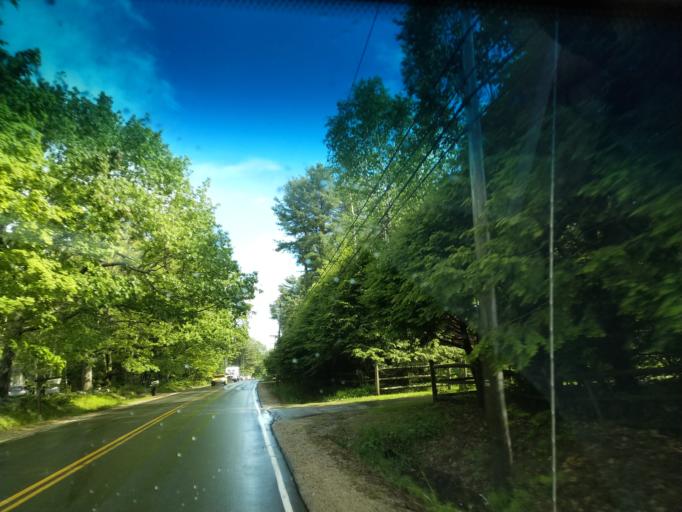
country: US
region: Maine
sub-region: Cumberland County
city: Cumberland Center
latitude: 43.7737
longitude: -70.3325
